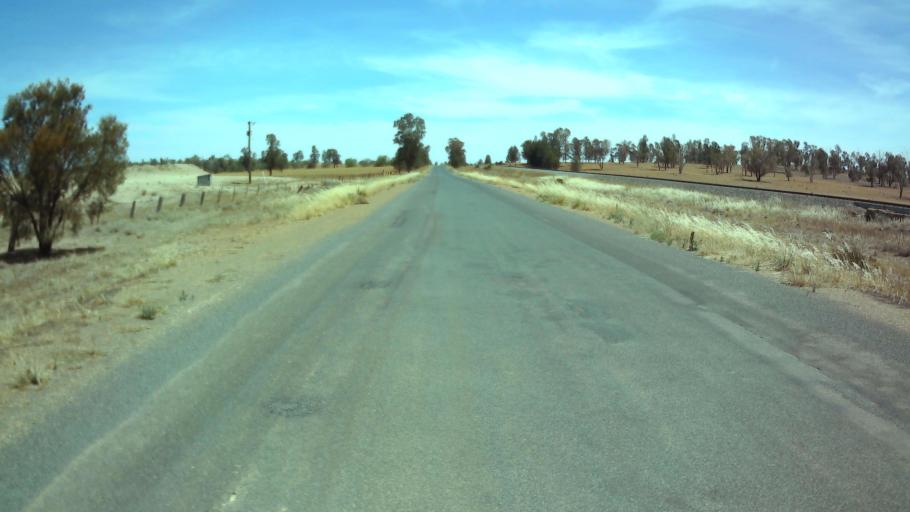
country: AU
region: New South Wales
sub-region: Weddin
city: Grenfell
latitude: -33.7678
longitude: 147.7582
